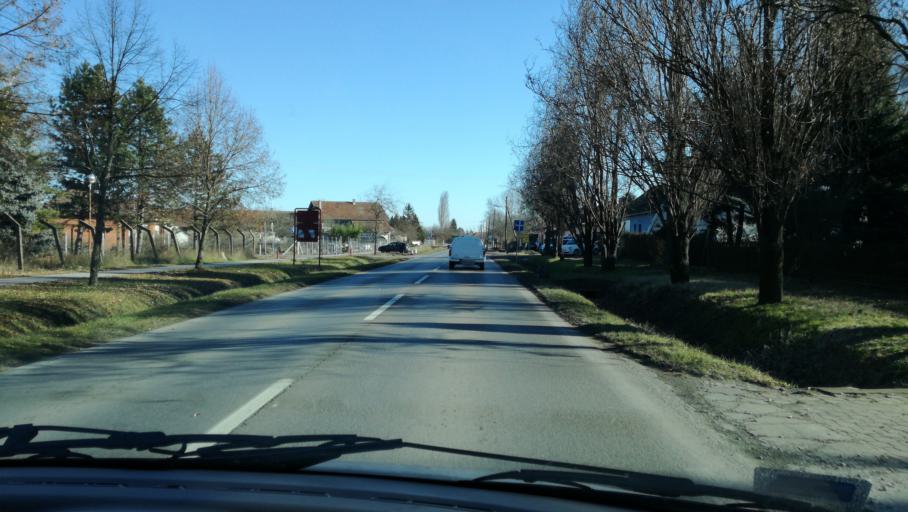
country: HU
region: Csongrad
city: Asotthalom
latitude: 46.1016
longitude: 19.7691
